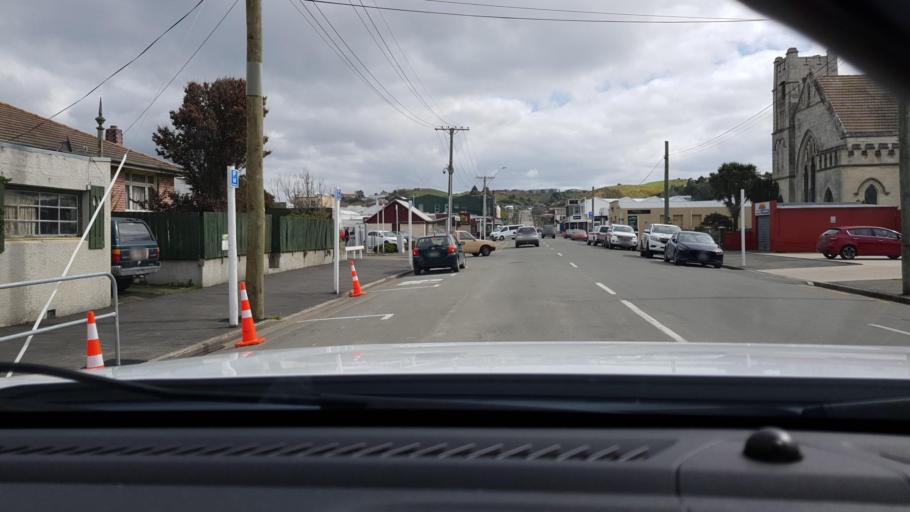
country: NZ
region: Otago
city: Oamaru
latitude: -45.0972
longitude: 170.9738
